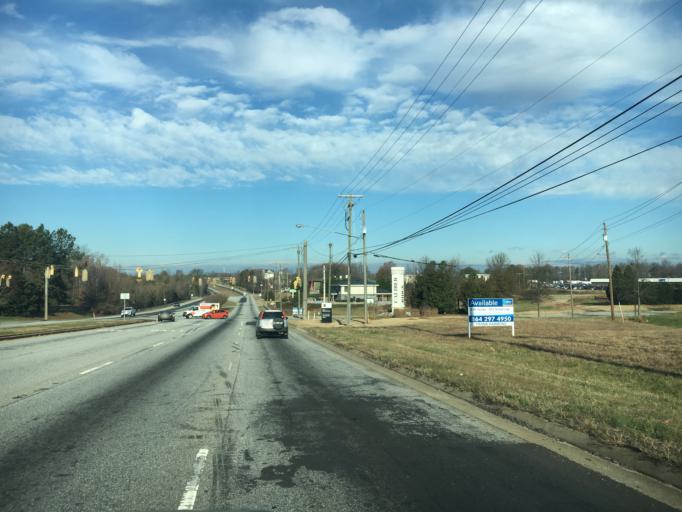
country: US
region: South Carolina
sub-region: Spartanburg County
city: Duncan
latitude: 34.8968
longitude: -82.1645
